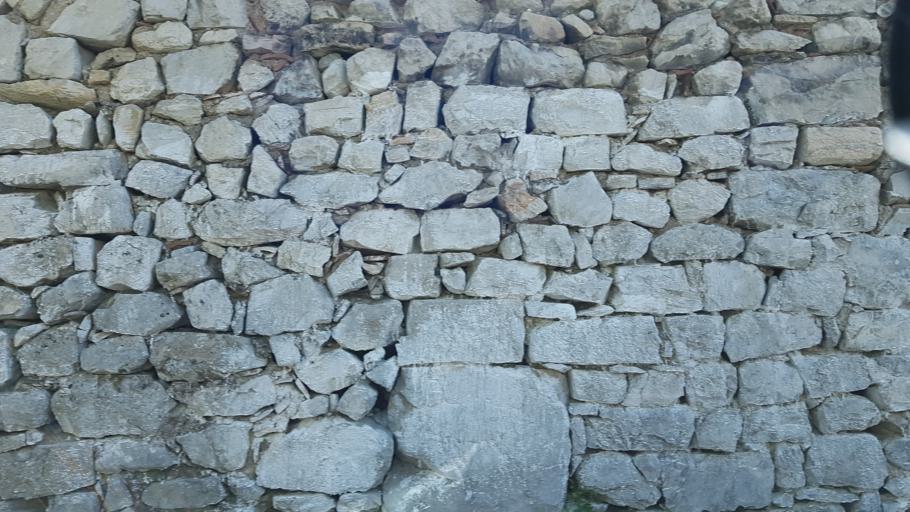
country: AL
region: Shkoder
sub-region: Rrethi i Shkodres
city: Guri i Zi
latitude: 42.1237
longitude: 19.6115
